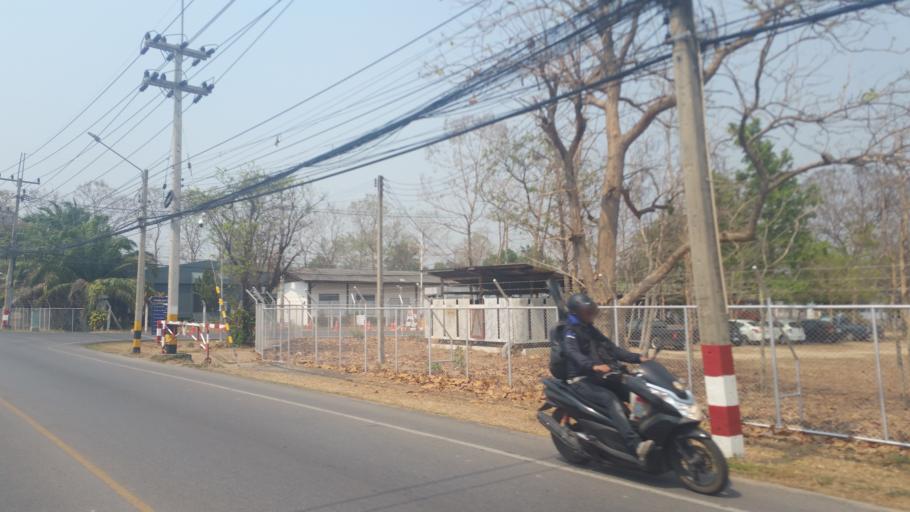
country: TH
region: Chiang Mai
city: Chiang Mai
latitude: 18.7773
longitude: 98.9671
